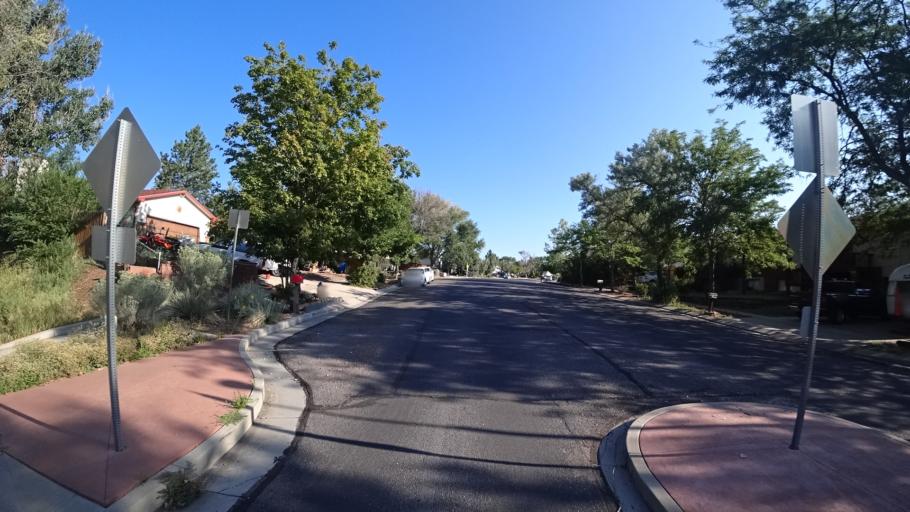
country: US
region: Colorado
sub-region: El Paso County
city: Colorado Springs
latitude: 38.8906
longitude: -104.8446
